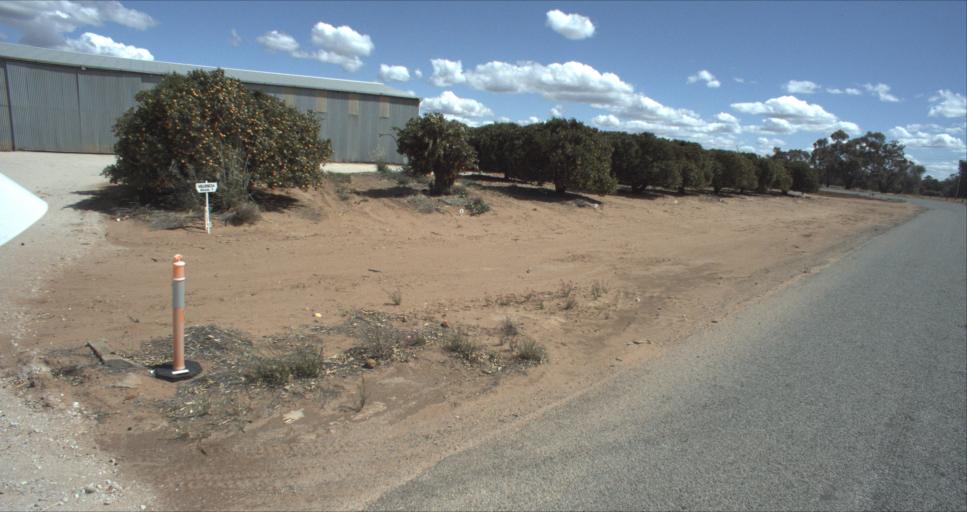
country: AU
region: New South Wales
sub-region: Leeton
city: Leeton
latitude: -34.5182
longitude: 146.2269
